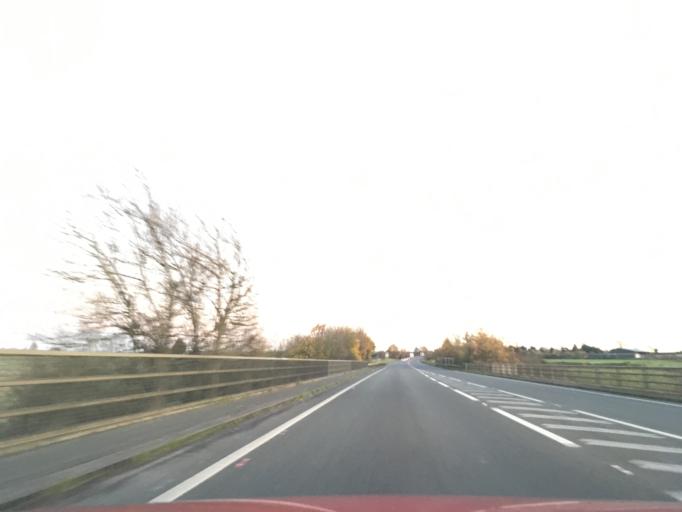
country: GB
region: England
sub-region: Worcestershire
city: Evesham
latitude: 52.1064
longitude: -1.9298
